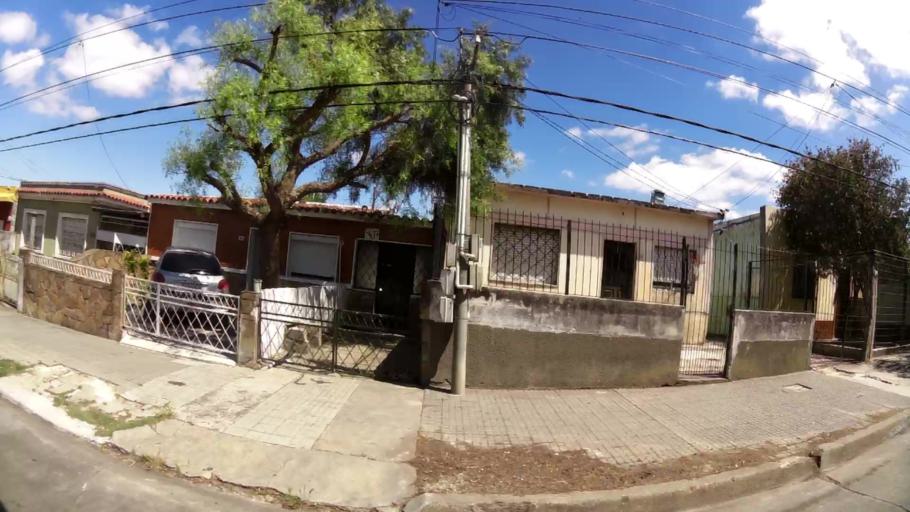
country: UY
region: Montevideo
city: Montevideo
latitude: -34.8579
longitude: -56.1382
